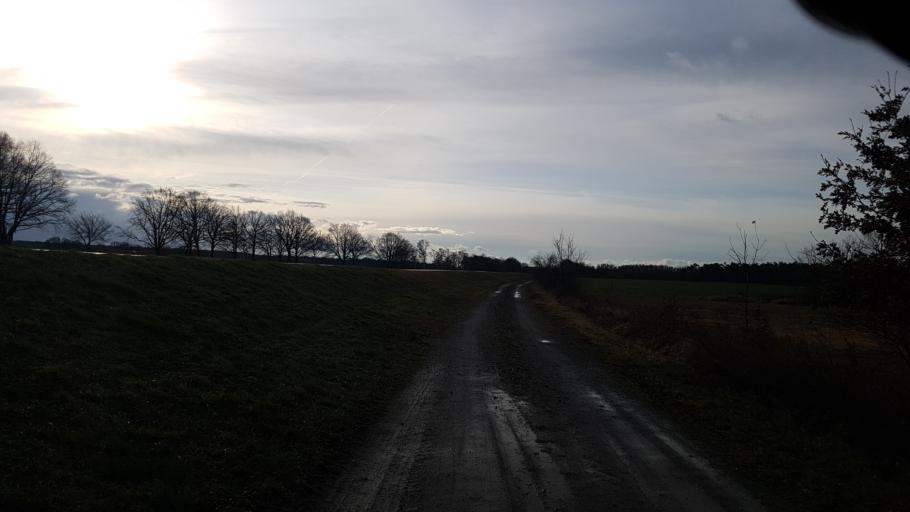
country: DE
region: Brandenburg
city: Herzberg
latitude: 51.6645
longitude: 13.2645
